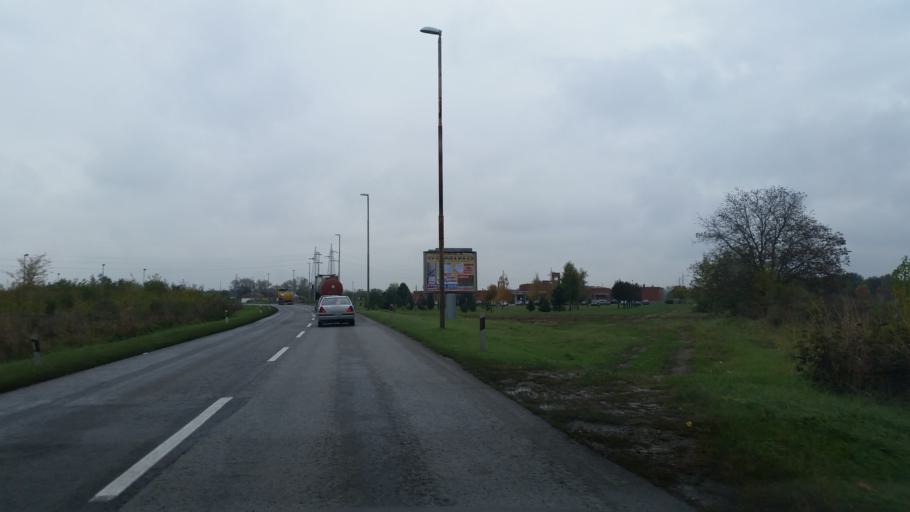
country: RS
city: Ecka
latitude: 45.3579
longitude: 20.4211
